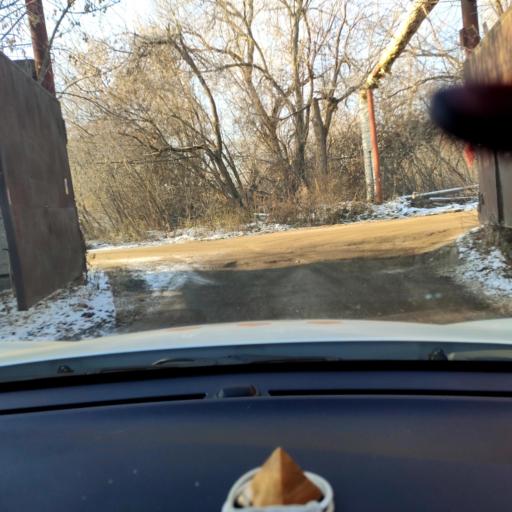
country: RU
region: Tatarstan
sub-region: Gorod Kazan'
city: Kazan
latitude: 55.8107
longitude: 49.0482
